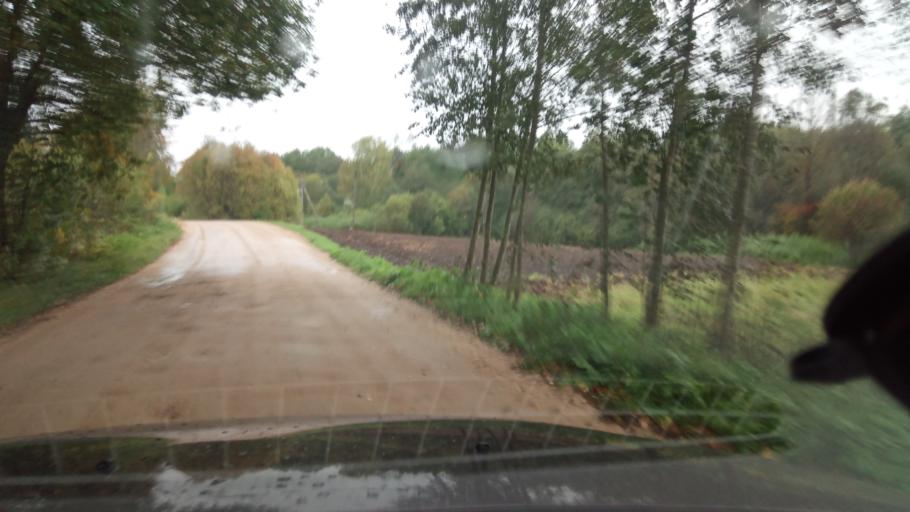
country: LT
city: Skaidiskes
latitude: 54.5565
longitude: 25.4891
